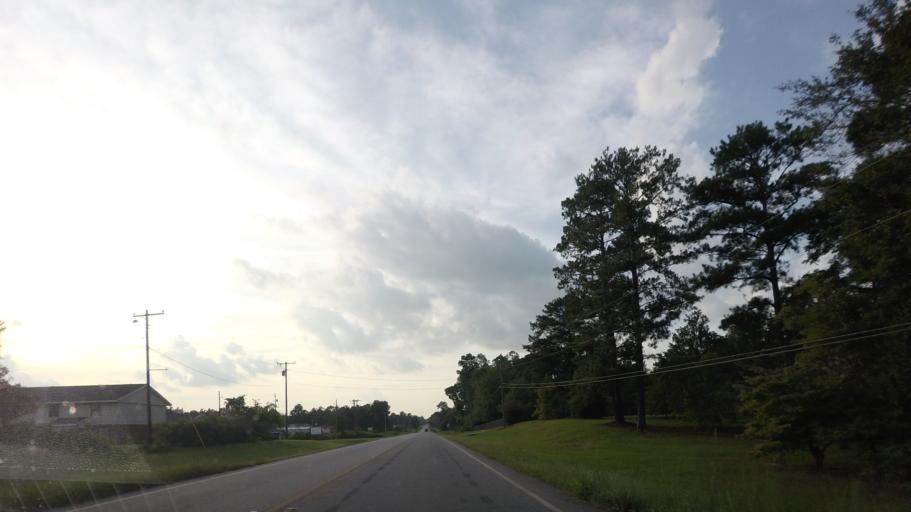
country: US
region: Georgia
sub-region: Wilkinson County
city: Gordon
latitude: 32.8893
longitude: -83.3521
